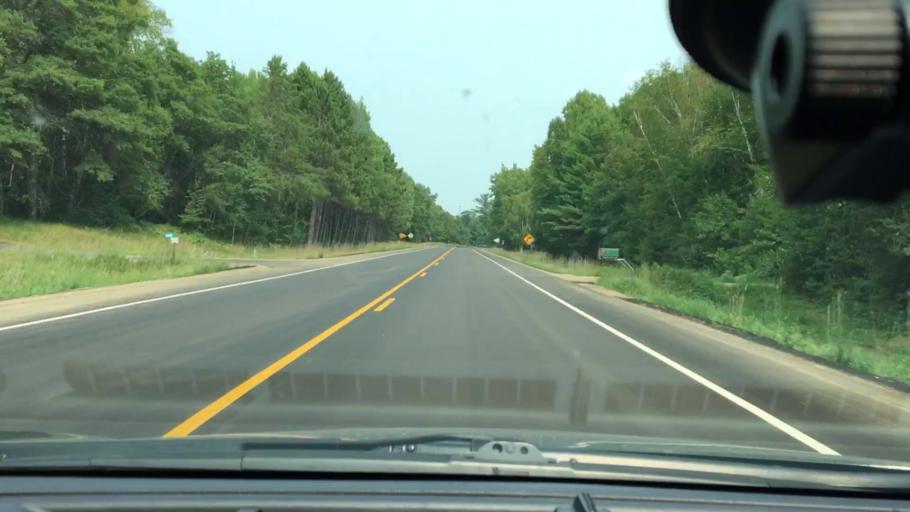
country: US
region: Minnesota
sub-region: Crow Wing County
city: Breezy Point
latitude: 46.5310
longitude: -94.2265
